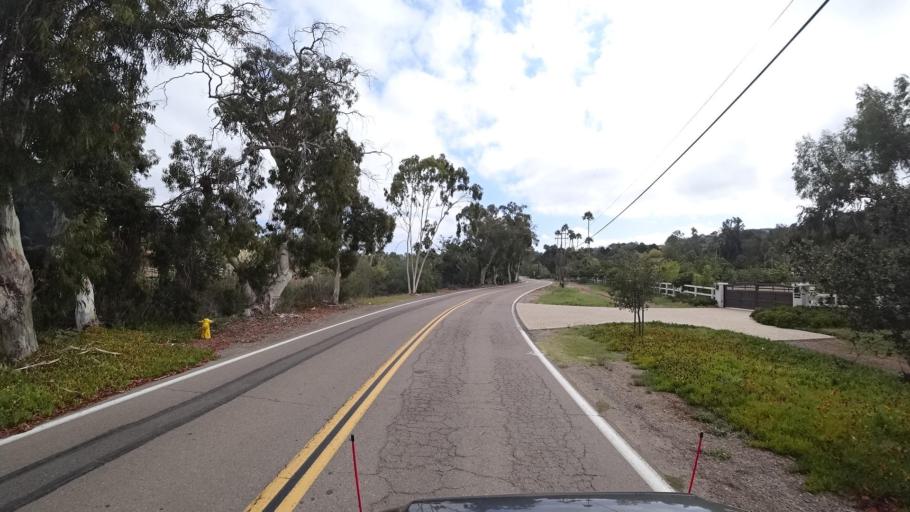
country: US
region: California
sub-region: San Diego County
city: Rancho Santa Fe
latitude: 33.0115
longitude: -117.2363
